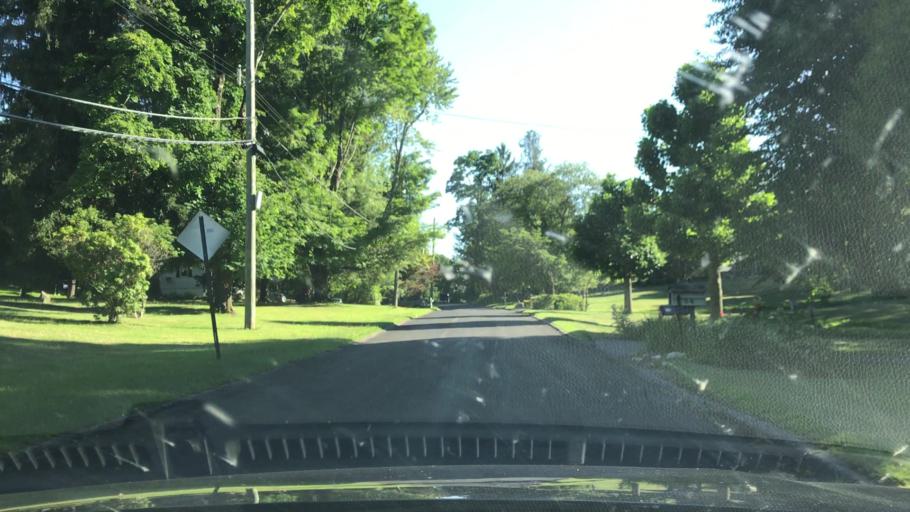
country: US
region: New York
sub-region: Westchester County
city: Thornwood
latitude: 41.1156
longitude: -73.7786
